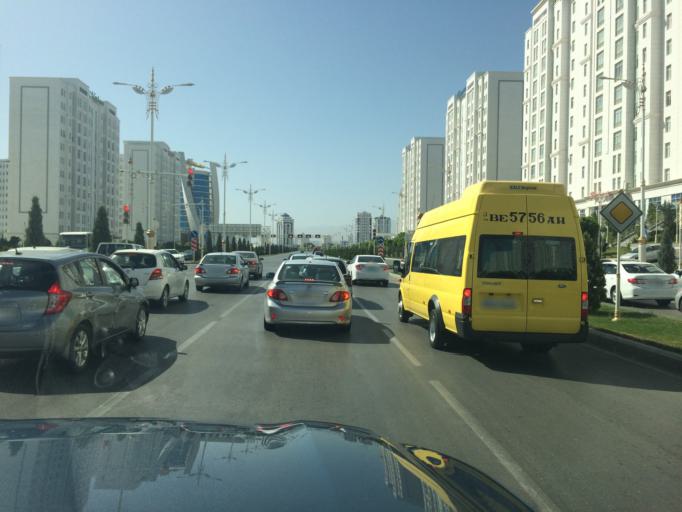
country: TM
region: Ahal
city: Ashgabat
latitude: 37.9342
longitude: 58.3666
